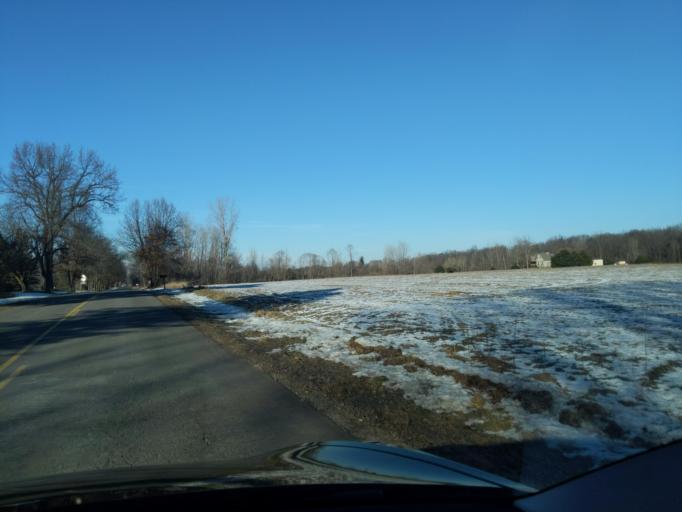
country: US
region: Michigan
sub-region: Ingham County
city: Stockbridge
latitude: 42.4398
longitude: -84.1505
